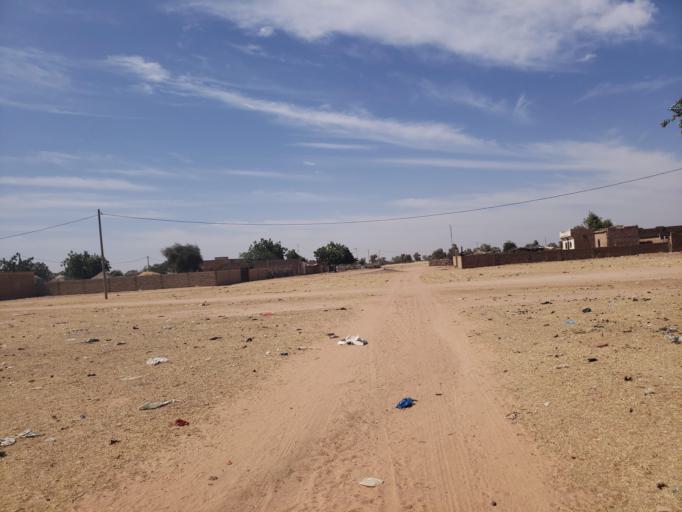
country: SN
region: Matam
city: Ranerou
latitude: 15.3030
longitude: -13.9610
